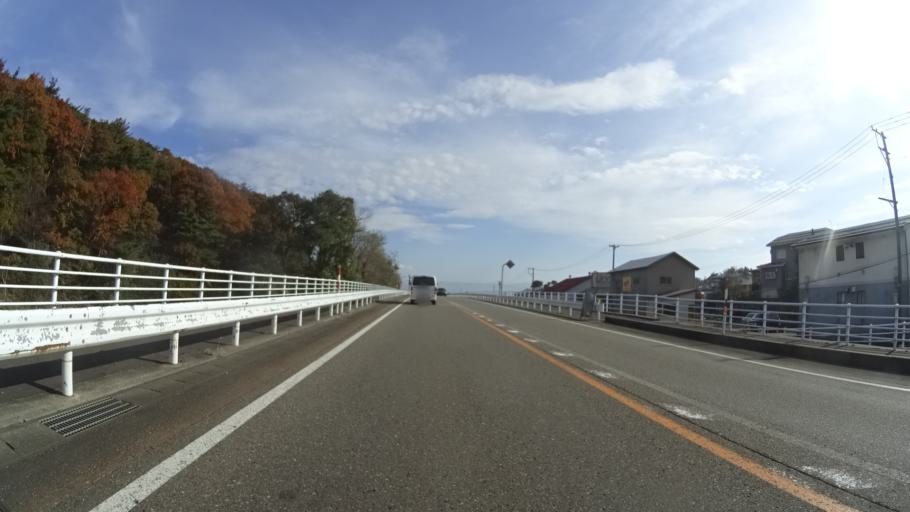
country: JP
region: Niigata
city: Joetsu
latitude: 37.1613
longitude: 138.2193
